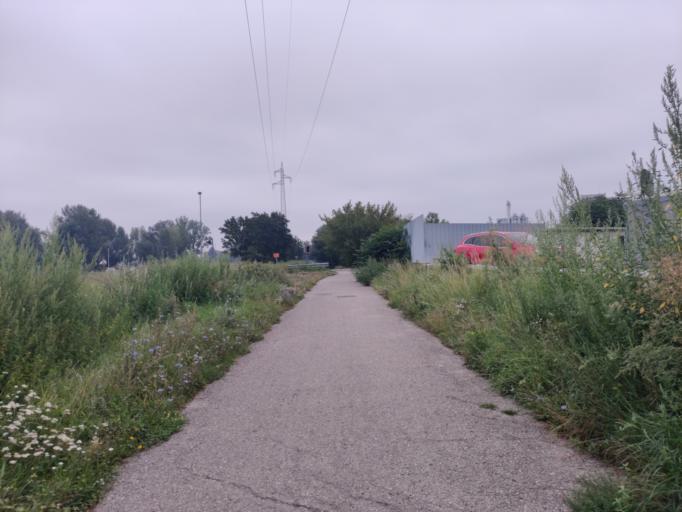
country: AT
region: Lower Austria
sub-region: Krems an der Donau Stadt
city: Krems an der Donau
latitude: 48.4100
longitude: 15.6292
